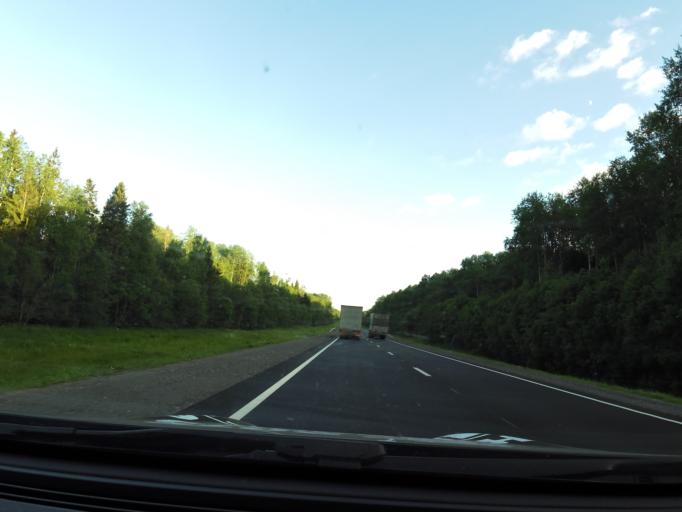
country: RU
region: Vologda
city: Gryazovets
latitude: 58.9326
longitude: 40.1758
